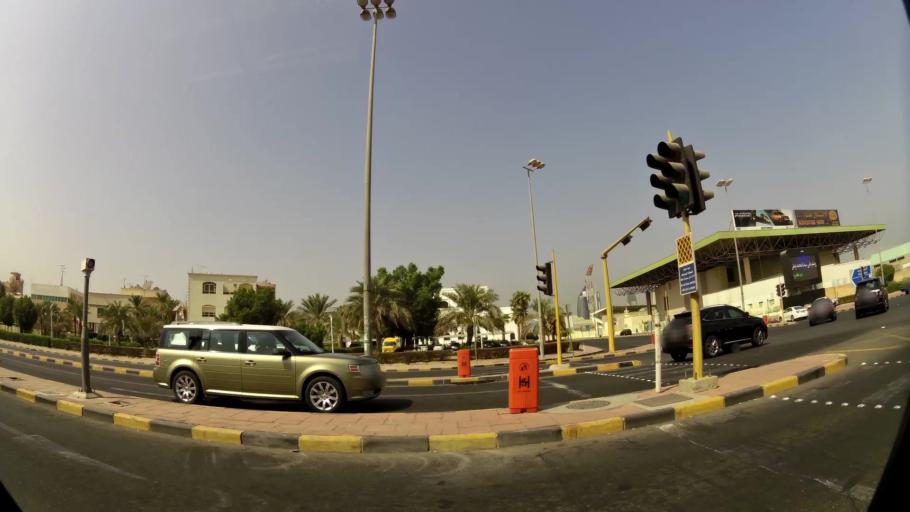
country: KW
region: Al Asimah
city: Ad Dasmah
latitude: 29.3544
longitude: 48.0003
